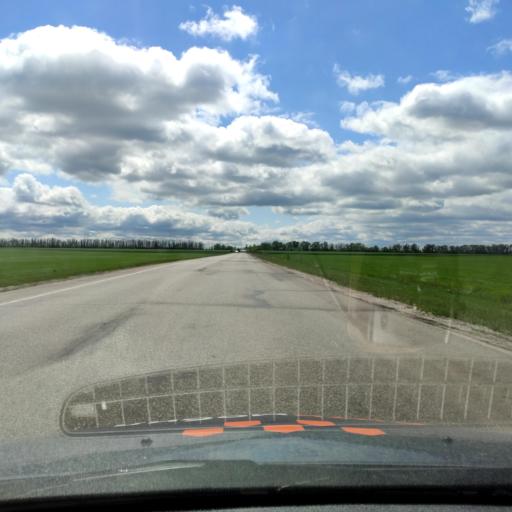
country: RU
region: Voronezj
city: Novaya Usman'
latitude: 51.5976
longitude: 39.3387
